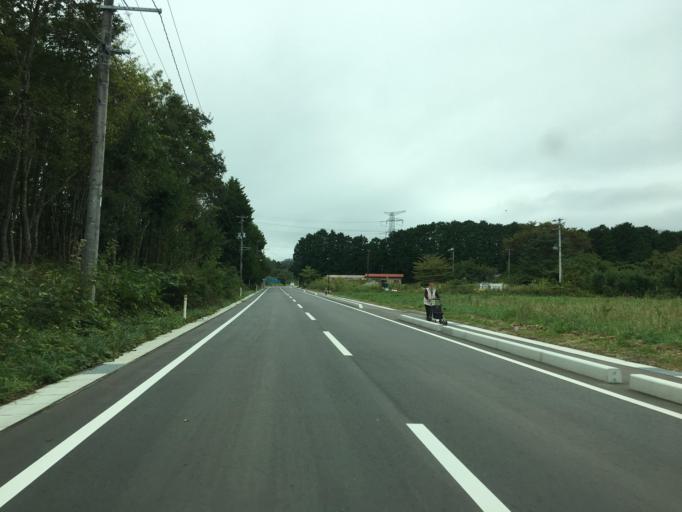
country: JP
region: Miyagi
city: Marumori
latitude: 37.8556
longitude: 140.9015
